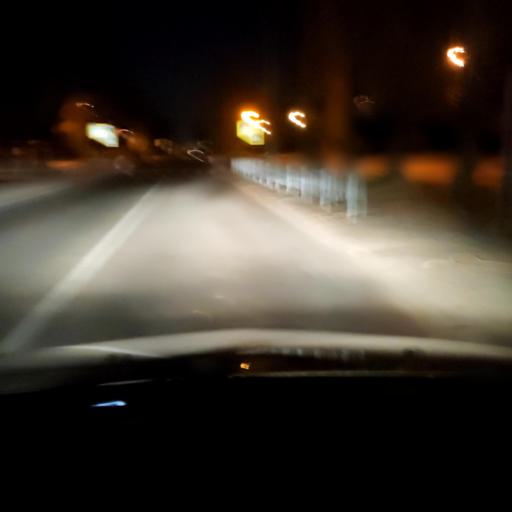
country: RU
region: Voronezj
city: Maslovka
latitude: 51.5514
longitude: 39.2354
